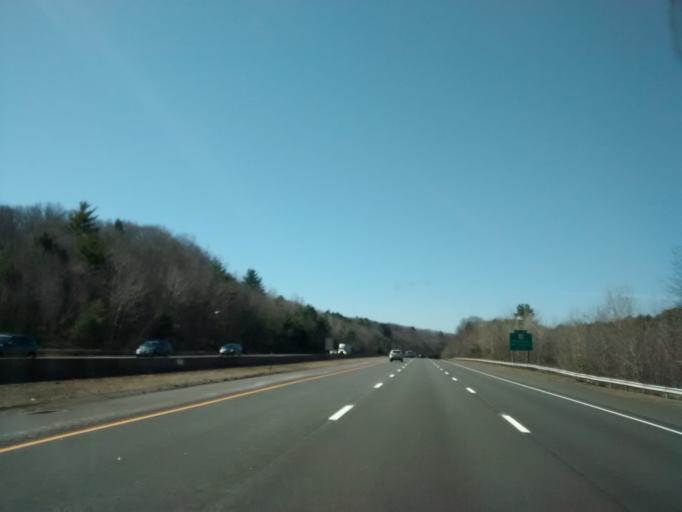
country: US
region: Connecticut
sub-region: Tolland County
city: Stafford Springs
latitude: 41.9114
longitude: -72.2700
